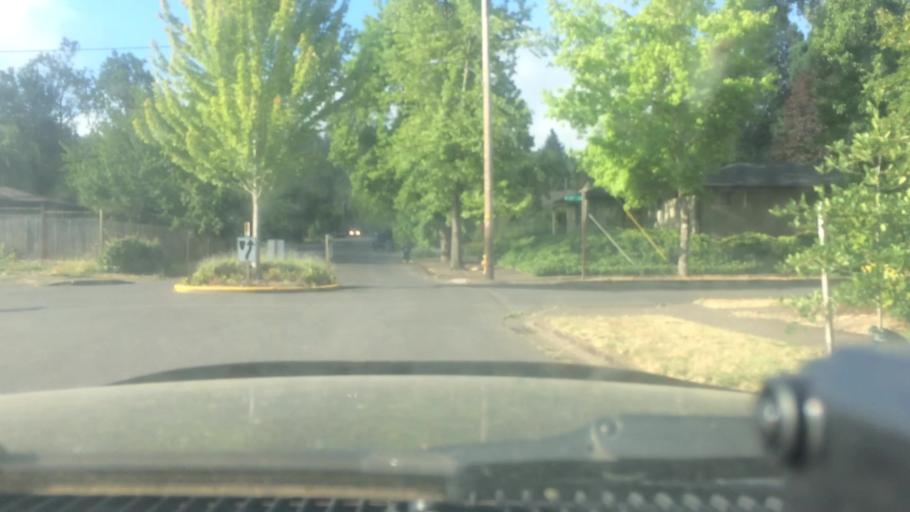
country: US
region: Oregon
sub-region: Lane County
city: Eugene
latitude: 44.0300
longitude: -123.1112
